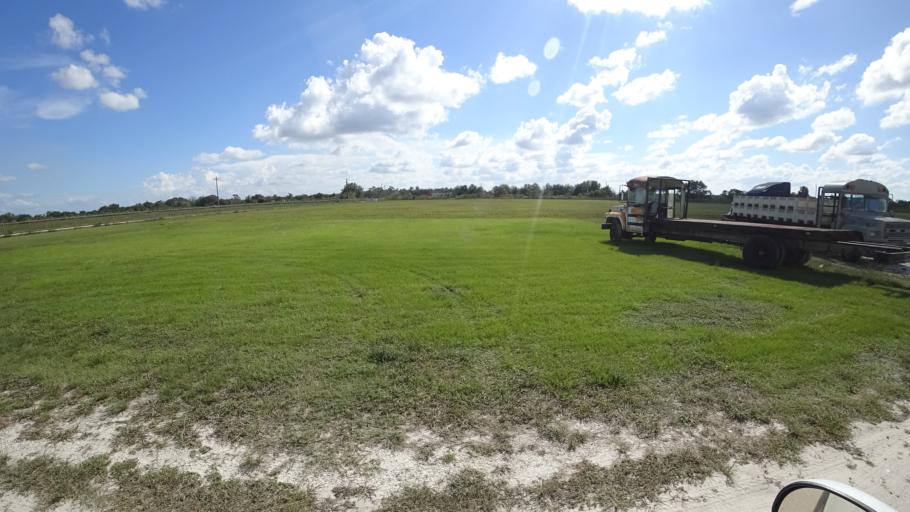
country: US
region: Florida
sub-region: DeSoto County
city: Arcadia
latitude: 27.3128
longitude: -82.1013
